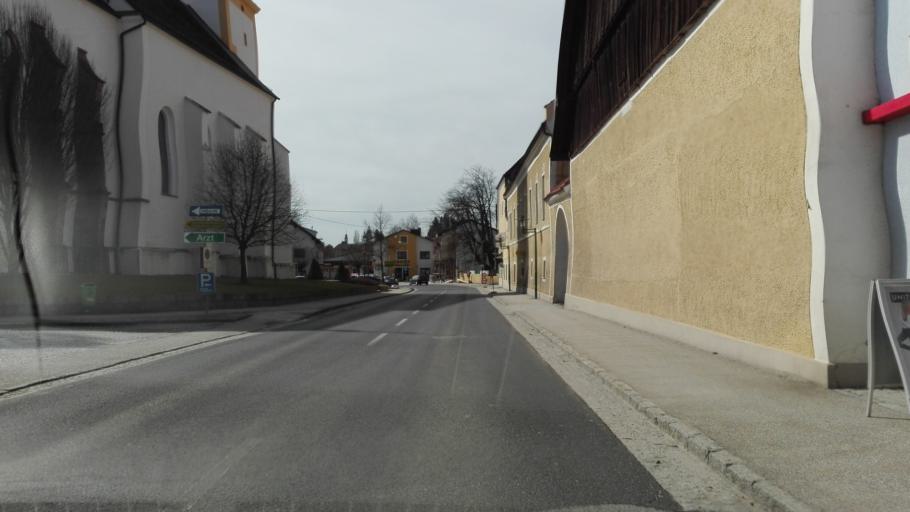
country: AT
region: Upper Austria
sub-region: Politischer Bezirk Scharding
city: Sankt Marienkirchen bei Schaerding
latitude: 48.3719
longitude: 13.5784
